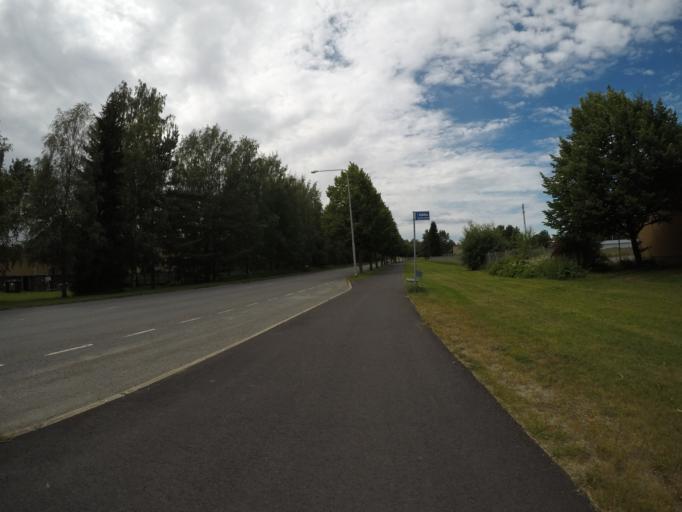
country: FI
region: Haeme
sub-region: Haemeenlinna
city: Parola
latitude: 61.0089
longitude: 24.4038
